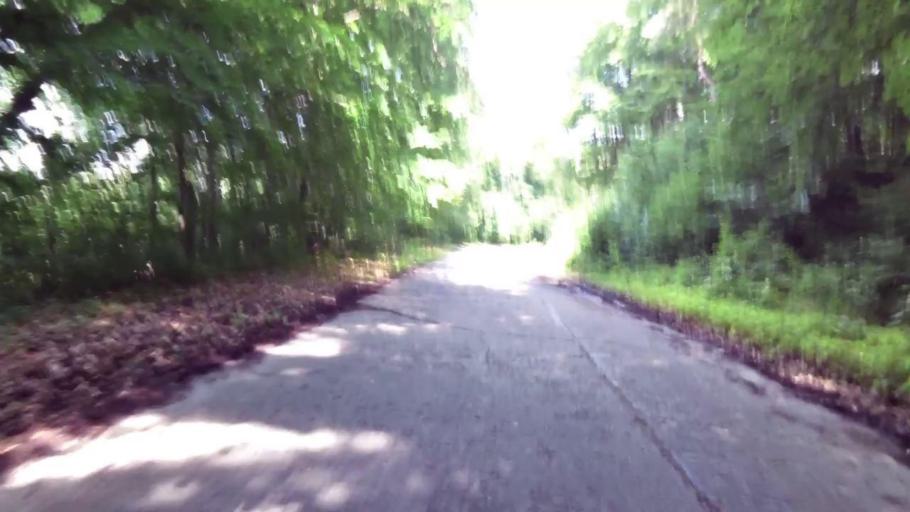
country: PL
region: West Pomeranian Voivodeship
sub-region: Powiat stargardzki
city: Insko
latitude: 53.4015
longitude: 15.5181
